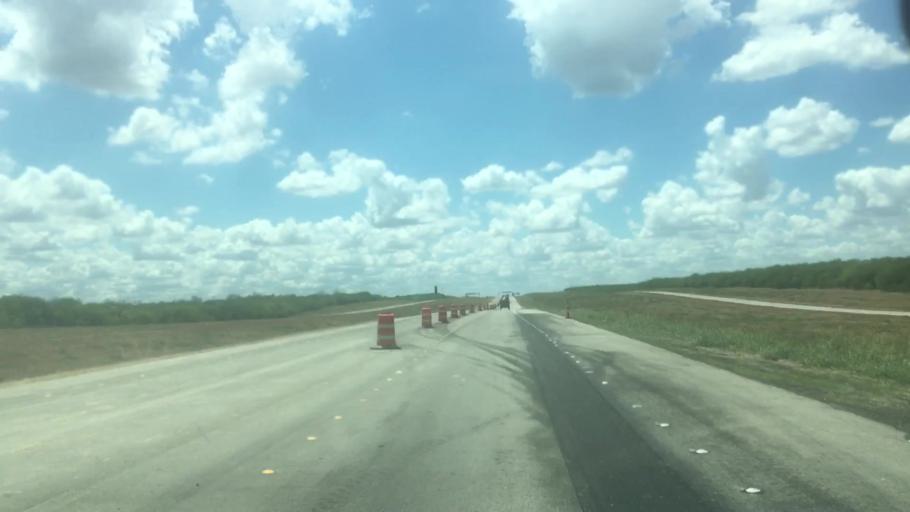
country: US
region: Texas
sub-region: Caldwell County
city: Martindale
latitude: 29.8230
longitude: -97.7515
